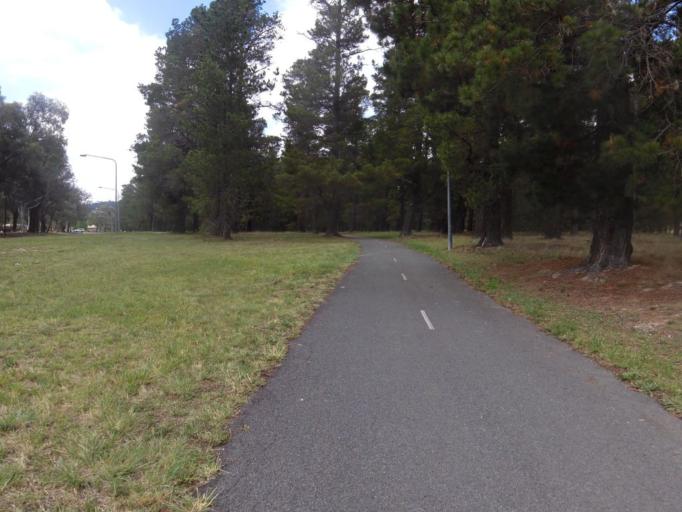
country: AU
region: Australian Capital Territory
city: Macarthur
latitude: -35.4137
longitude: 149.1168
